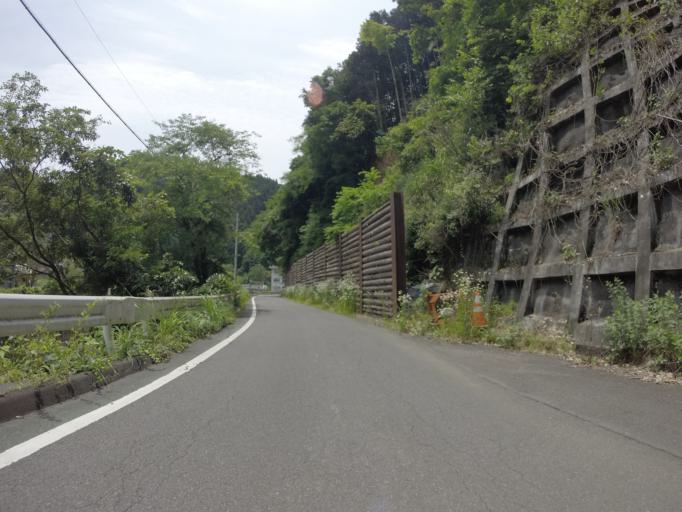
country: JP
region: Shizuoka
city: Shizuoka-shi
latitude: 35.0397
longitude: 138.2951
